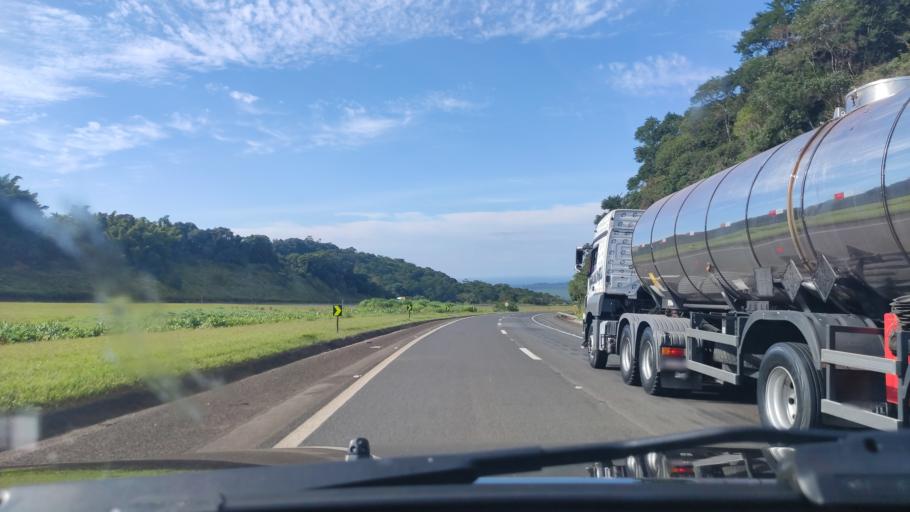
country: BR
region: Sao Paulo
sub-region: Itatinga
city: Itatinga
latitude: -23.0900
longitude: -48.5068
